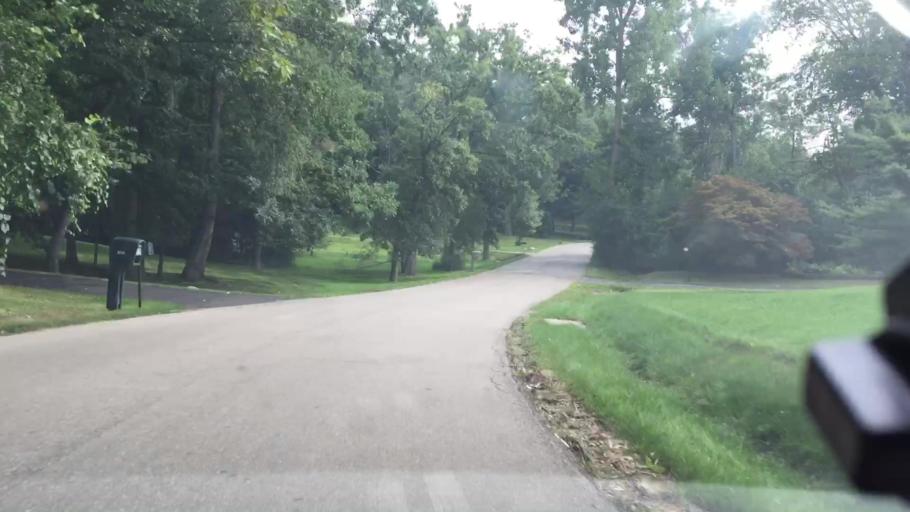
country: US
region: Michigan
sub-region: Oakland County
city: Sylvan Lake
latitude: 42.5984
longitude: -83.2914
